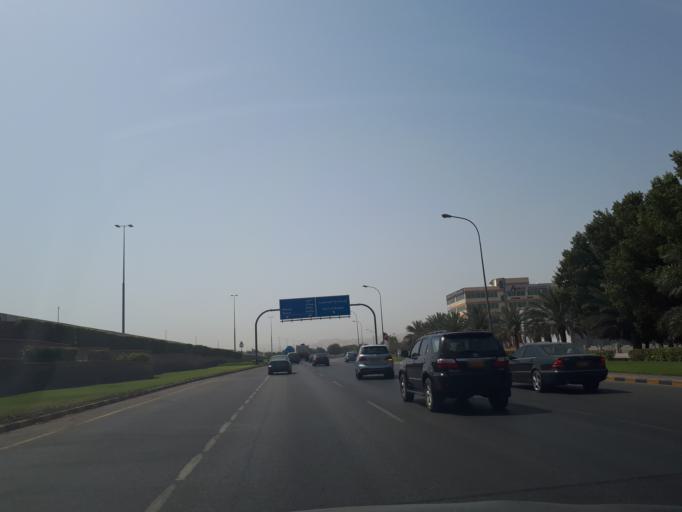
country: OM
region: Muhafazat Masqat
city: As Sib al Jadidah
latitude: 23.6110
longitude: 58.2458
